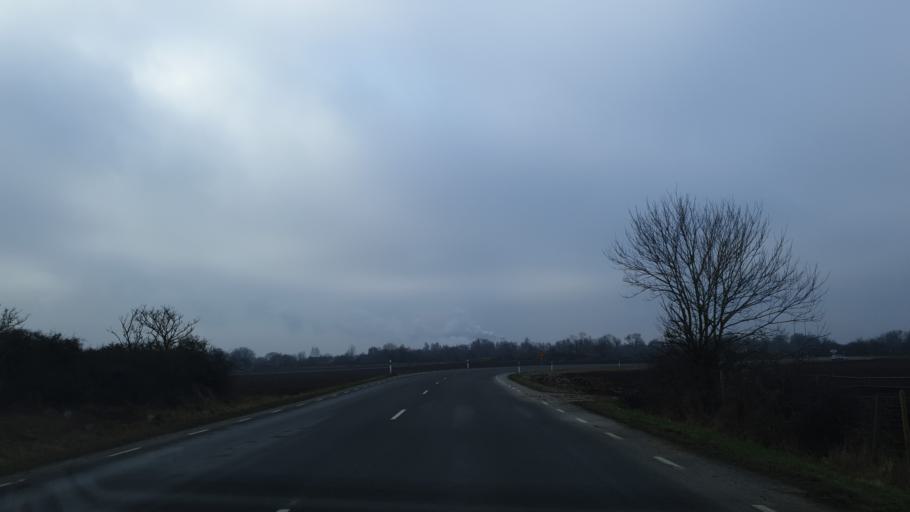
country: SE
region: Skane
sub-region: Bromolla Kommun
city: Bromoella
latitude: 56.0615
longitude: 14.5034
